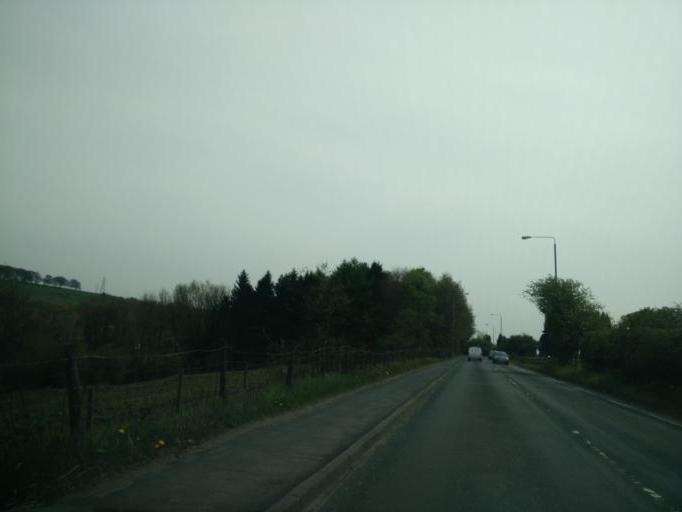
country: GB
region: England
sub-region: County Durham
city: Crook
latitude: 54.6994
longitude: -1.7495
